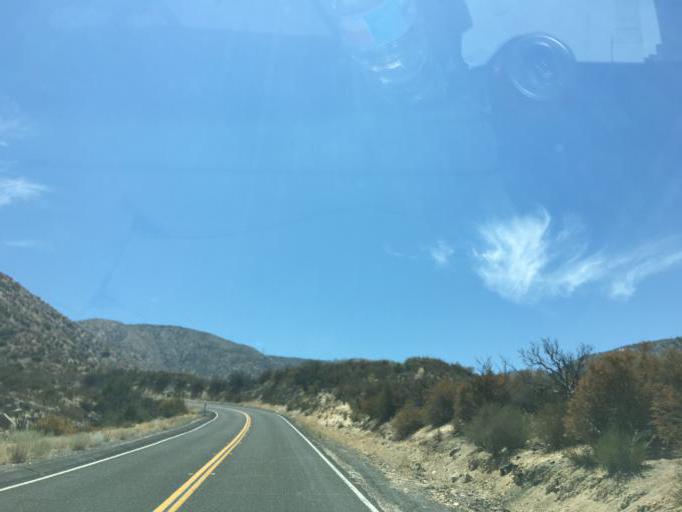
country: US
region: California
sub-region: Los Angeles County
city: Vincent
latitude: 34.4161
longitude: -118.0913
